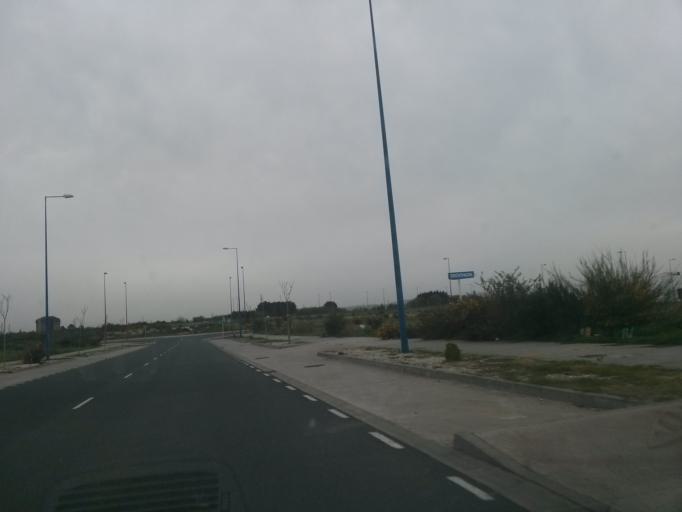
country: ES
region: Galicia
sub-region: Provincia de Lugo
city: Lugo
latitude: 43.0385
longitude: -7.5505
